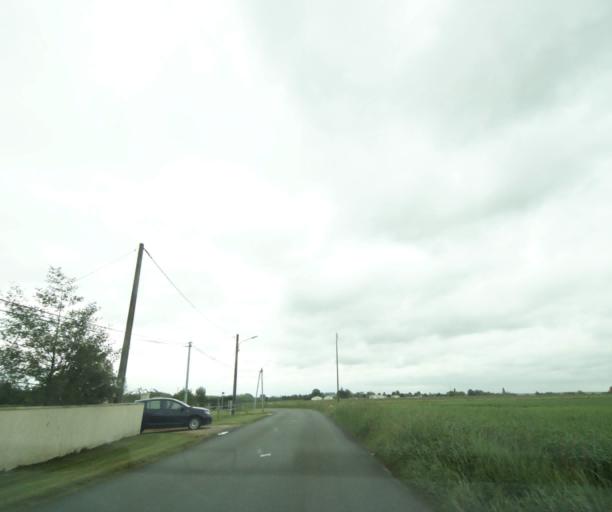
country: FR
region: Poitou-Charentes
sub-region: Departement de la Charente-Maritime
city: Chaniers
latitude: 45.7039
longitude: -0.5619
